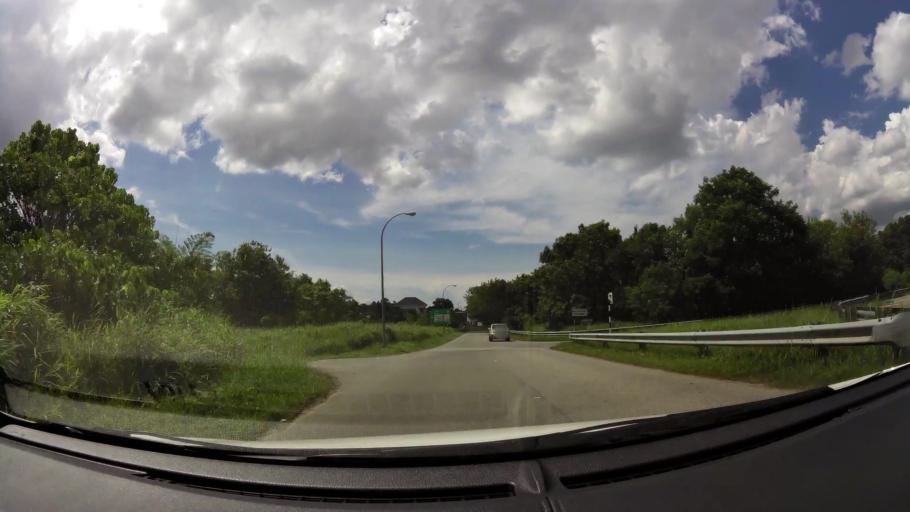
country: BN
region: Brunei and Muara
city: Bandar Seri Begawan
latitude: 4.9498
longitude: 114.9507
